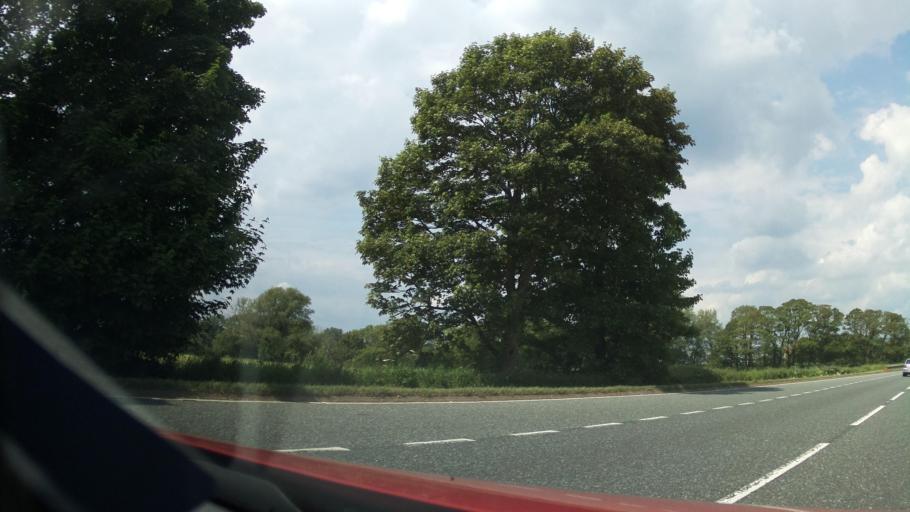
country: GB
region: England
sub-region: North Yorkshire
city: Thirsk
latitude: 54.2576
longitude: -1.3487
